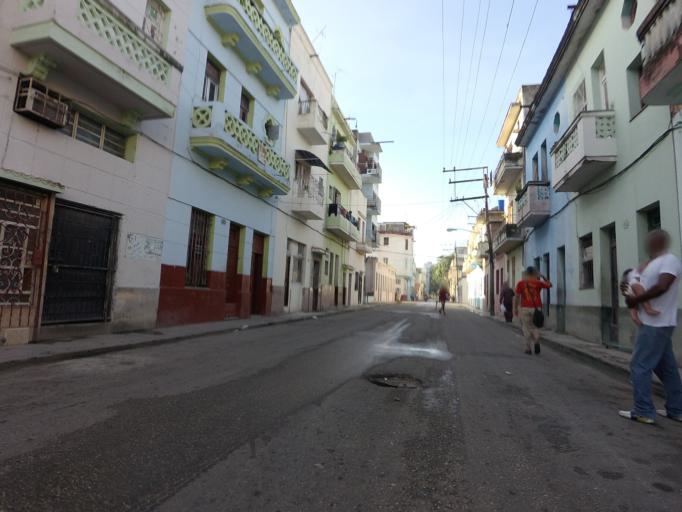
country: CU
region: La Habana
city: Havana
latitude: 23.1264
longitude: -82.3723
